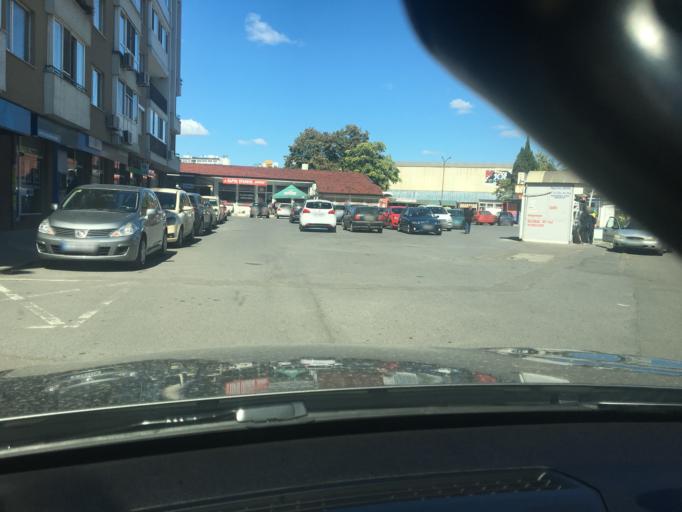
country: BG
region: Burgas
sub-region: Obshtina Burgas
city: Burgas
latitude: 42.5238
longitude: 27.4653
